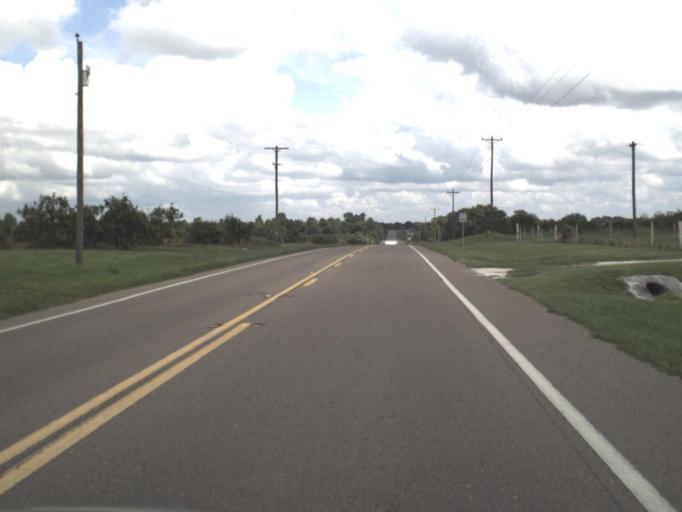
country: US
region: Florida
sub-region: Hardee County
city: Zolfo Springs
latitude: 27.4822
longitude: -81.8705
